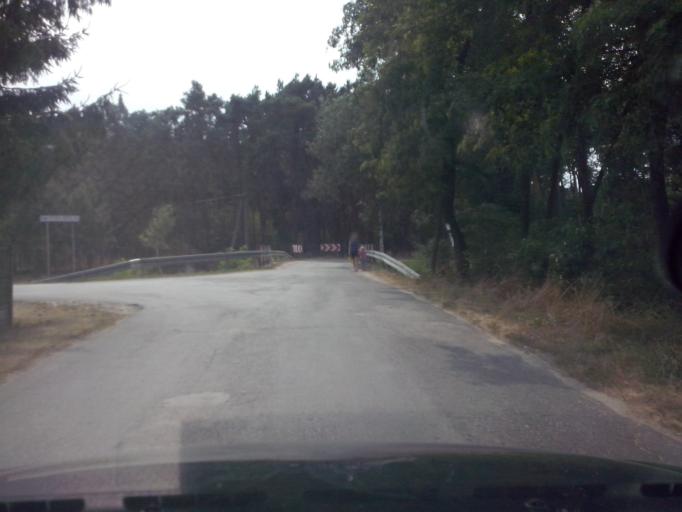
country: PL
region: Swietokrzyskie
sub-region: Powiat kielecki
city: Brzeziny
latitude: 50.7552
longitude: 20.5227
